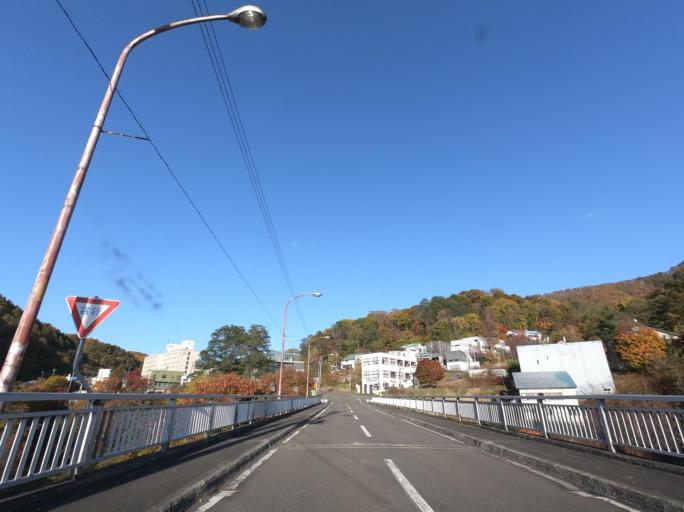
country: JP
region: Hokkaido
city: Iwamizawa
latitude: 43.0571
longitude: 141.9756
